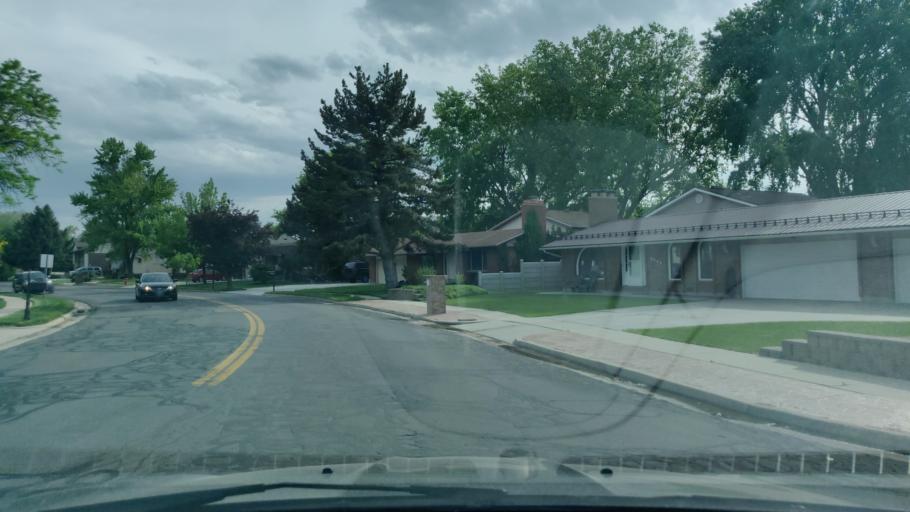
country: US
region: Utah
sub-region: Salt Lake County
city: Little Cottonwood Creek Valley
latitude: 40.6297
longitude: -111.8528
